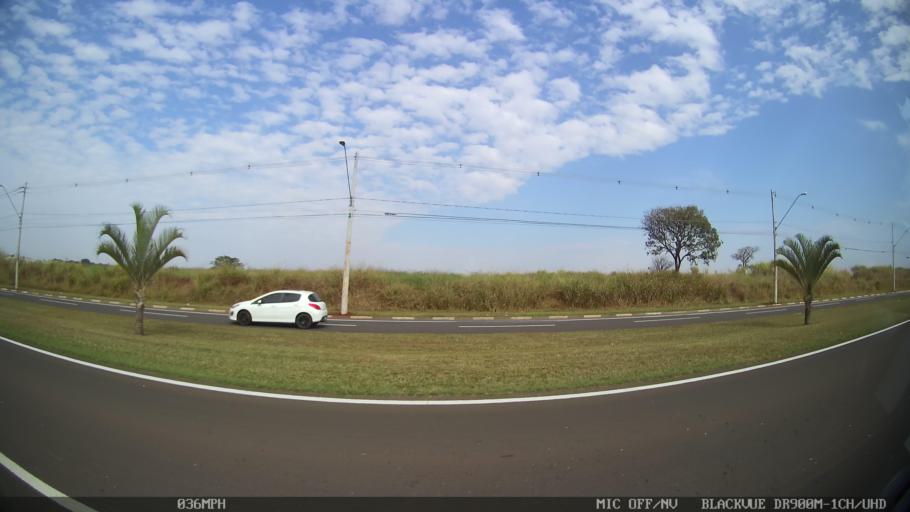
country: BR
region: Sao Paulo
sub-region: Paulinia
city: Paulinia
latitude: -22.7942
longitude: -47.1489
